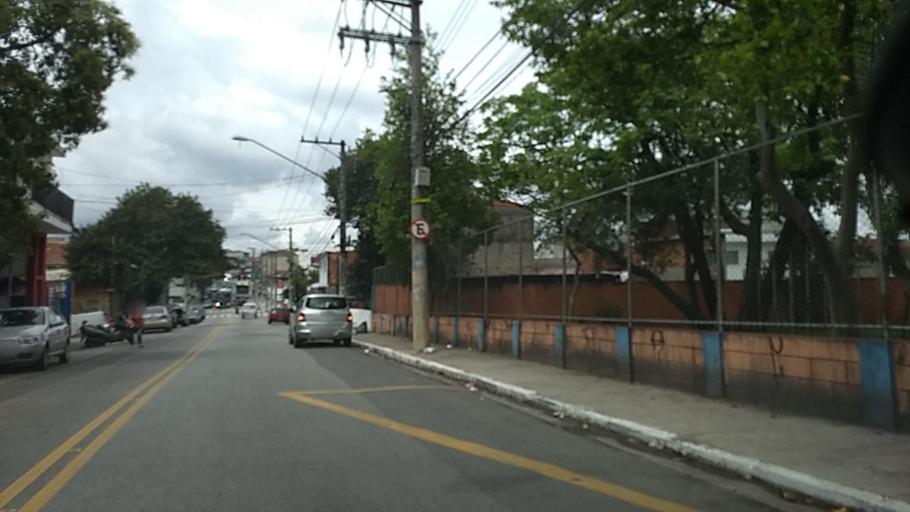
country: BR
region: Sao Paulo
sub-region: Guarulhos
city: Guarulhos
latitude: -23.4779
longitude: -46.5839
